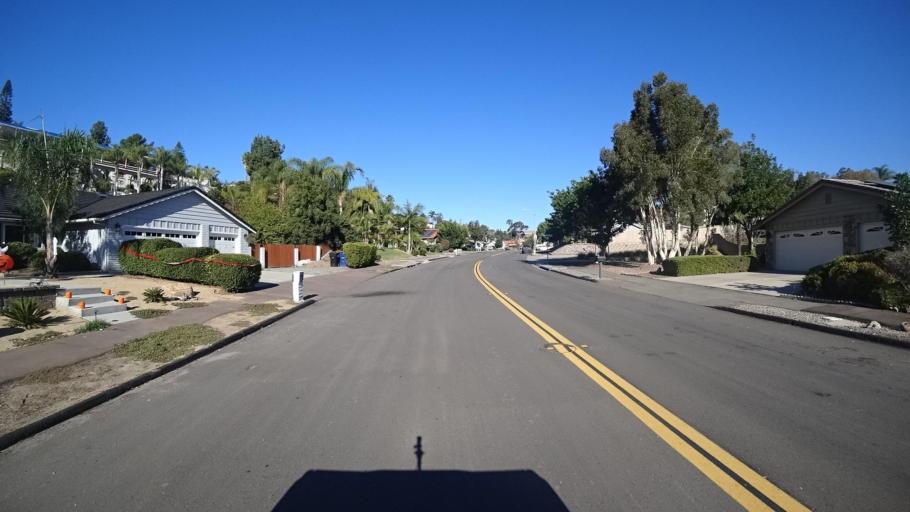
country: US
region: California
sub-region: San Diego County
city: Bonita
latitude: 32.6833
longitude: -117.0187
